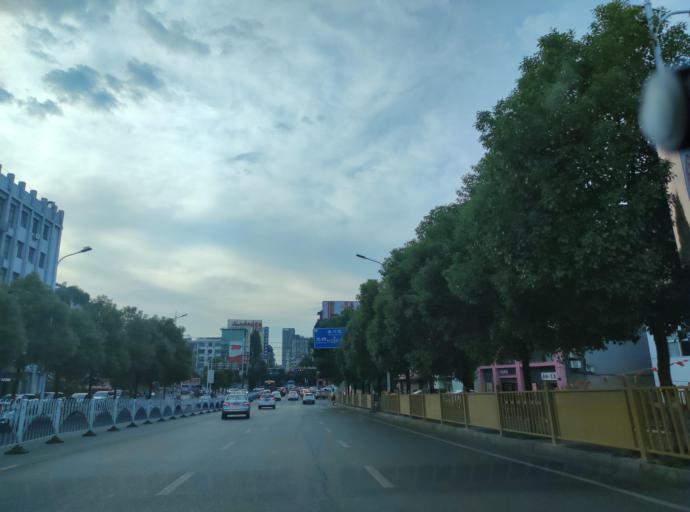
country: CN
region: Jiangxi Sheng
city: Pingxiang
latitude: 27.6342
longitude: 113.8582
